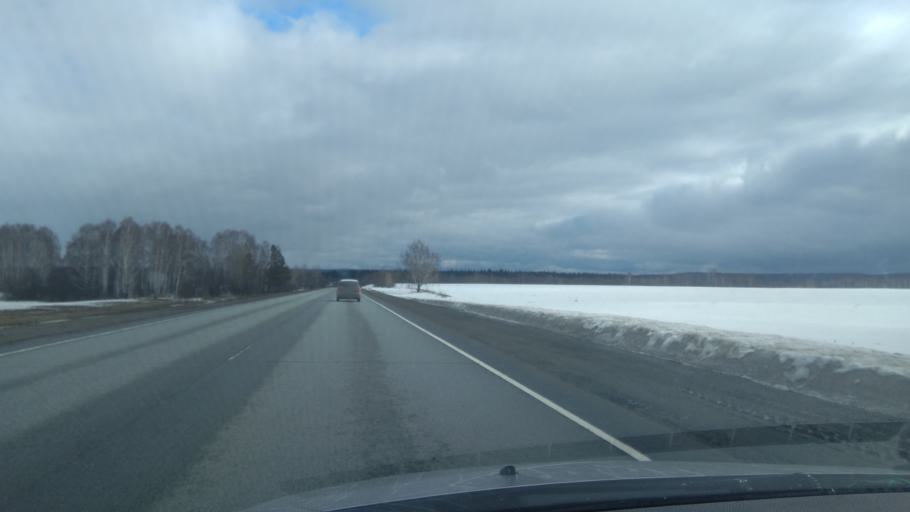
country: RU
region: Sverdlovsk
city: Ufimskiy
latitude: 56.7724
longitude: 58.0728
